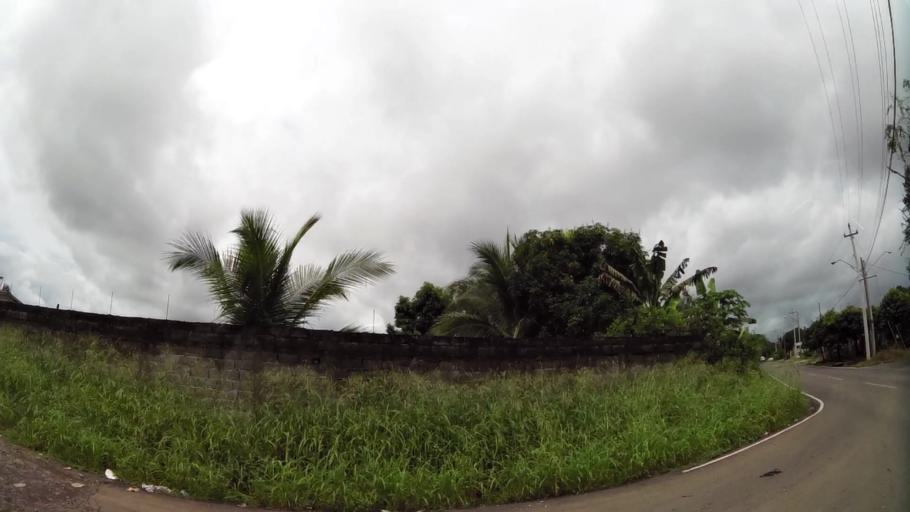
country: PA
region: Chiriqui
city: David
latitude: 8.4145
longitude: -82.4528
